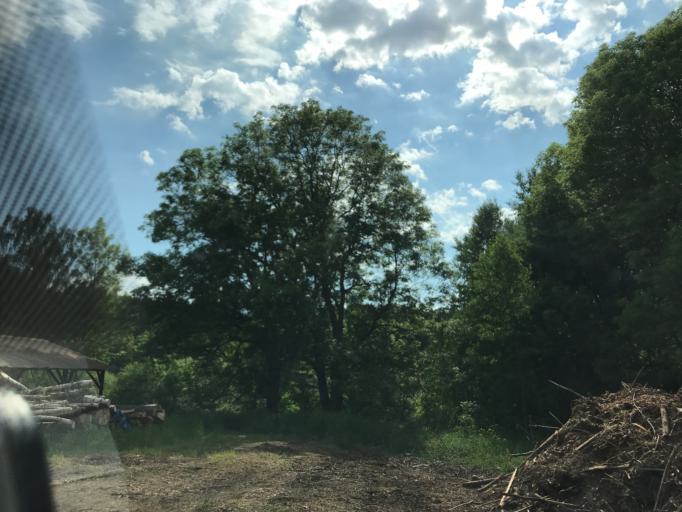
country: SE
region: Stockholm
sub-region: Solna Kommun
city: Rasunda
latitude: 59.4062
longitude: 17.9882
